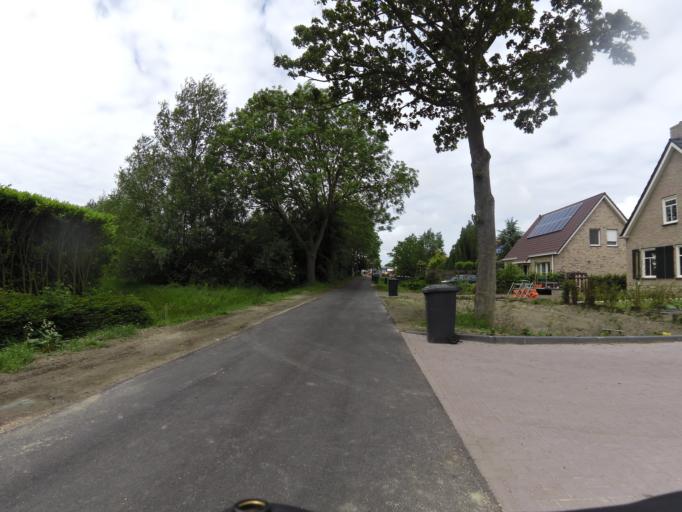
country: NL
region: Zeeland
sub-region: Schouwen-Duiveland
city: Scharendijke
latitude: 51.6462
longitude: 3.9354
